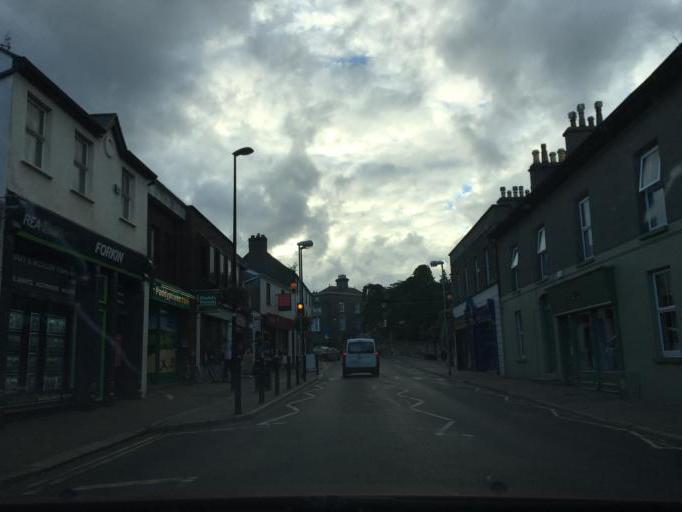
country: IE
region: Leinster
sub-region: Wicklow
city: Wicklow
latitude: 52.9808
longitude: -6.0442
